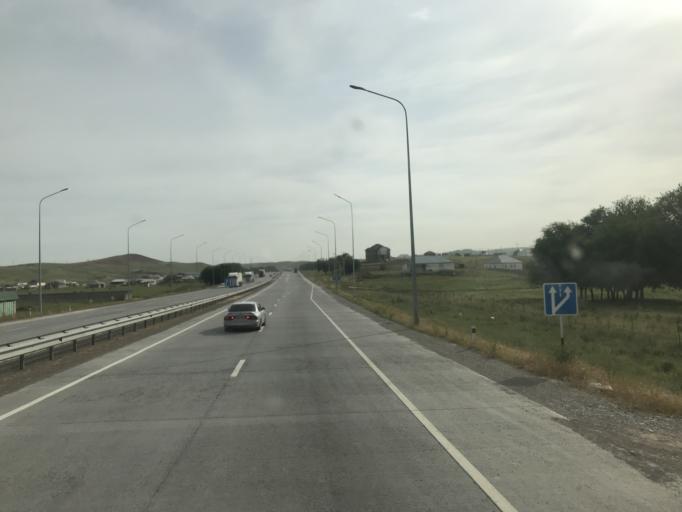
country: KZ
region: Ongtustik Qazaqstan
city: Shymkent
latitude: 42.2109
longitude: 69.5187
